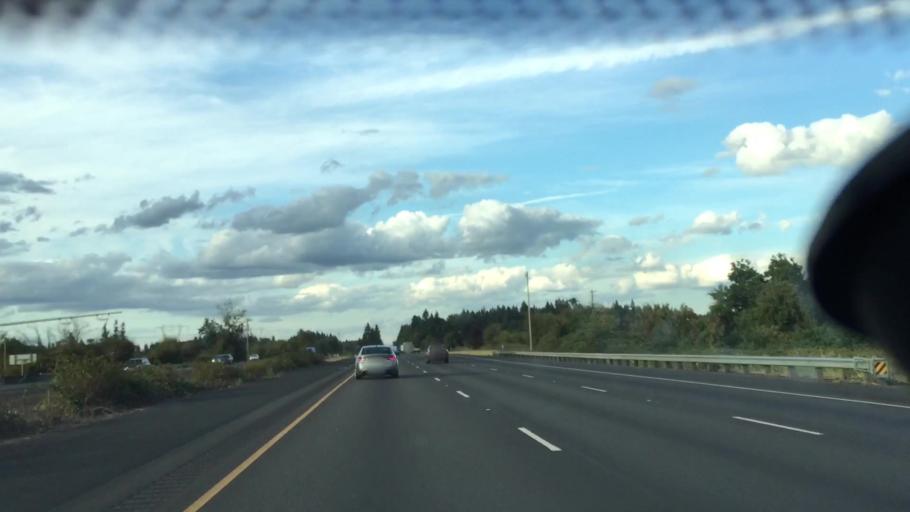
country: US
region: Oregon
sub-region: Marion County
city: Hubbard
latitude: 45.1993
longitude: -122.8329
